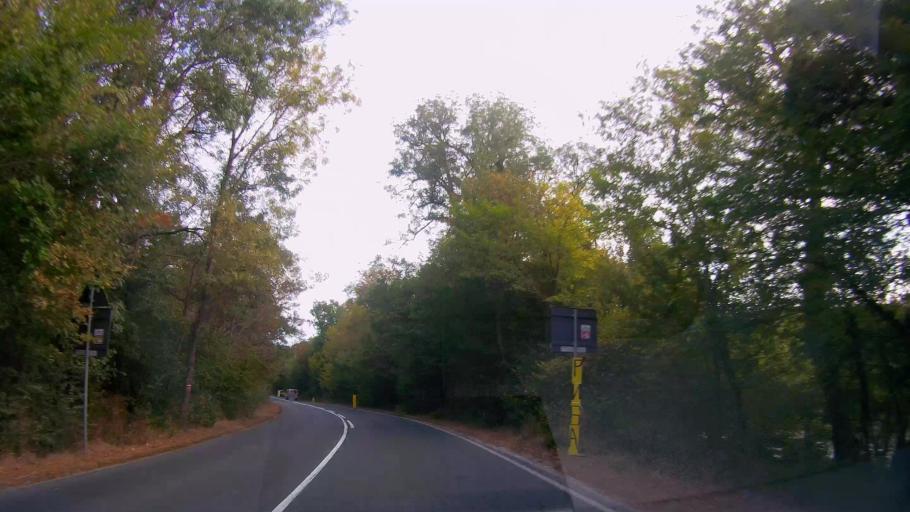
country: BG
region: Burgas
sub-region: Obshtina Primorsko
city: Primorsko
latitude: 42.3062
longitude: 27.7229
